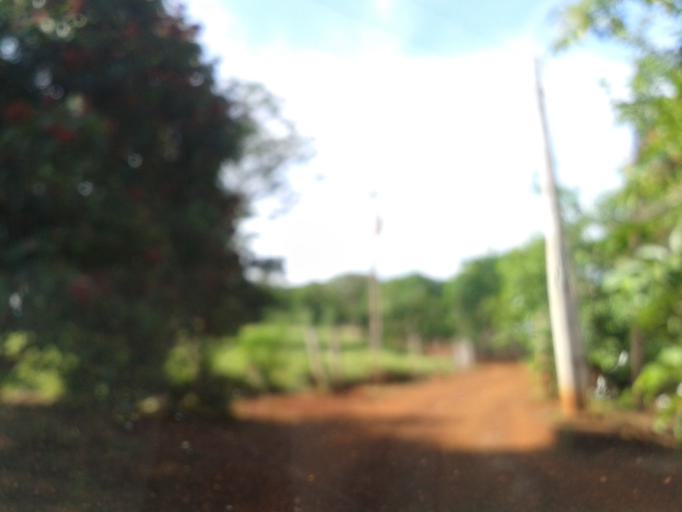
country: BR
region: Minas Gerais
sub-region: Centralina
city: Centralina
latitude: -18.7066
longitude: -49.1958
